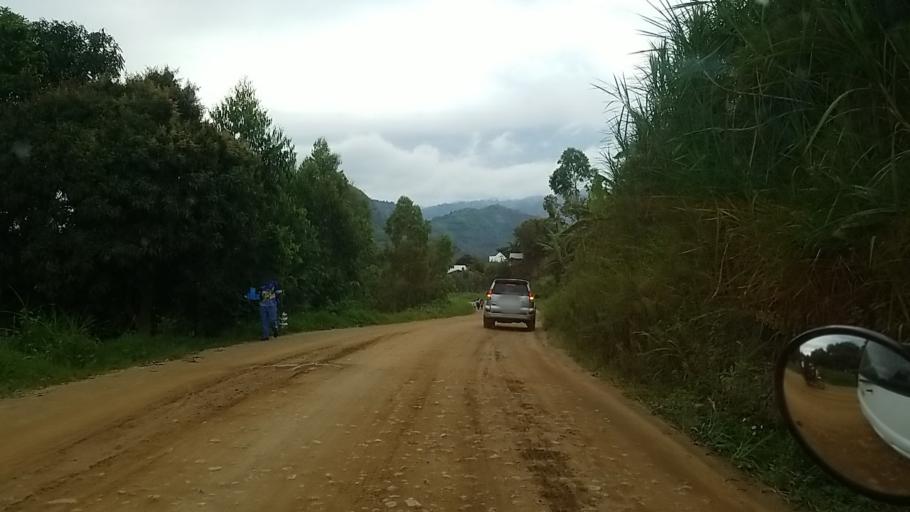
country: CD
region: Nord Kivu
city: Sake
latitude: -1.6753
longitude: 29.0179
